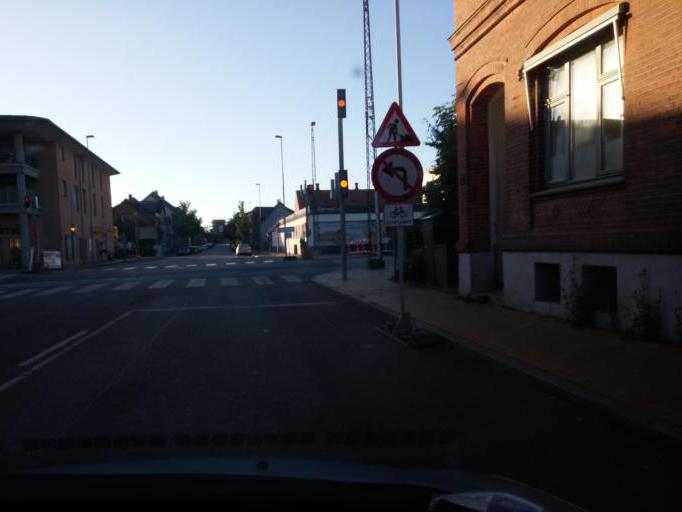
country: DK
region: South Denmark
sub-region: Odense Kommune
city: Odense
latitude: 55.3954
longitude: 10.3704
